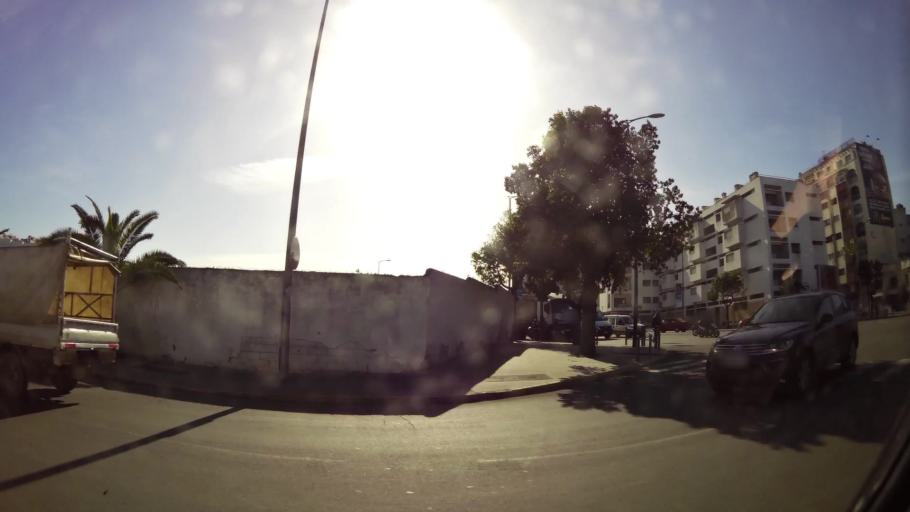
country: MA
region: Grand Casablanca
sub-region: Casablanca
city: Casablanca
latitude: 33.5977
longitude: -7.5914
